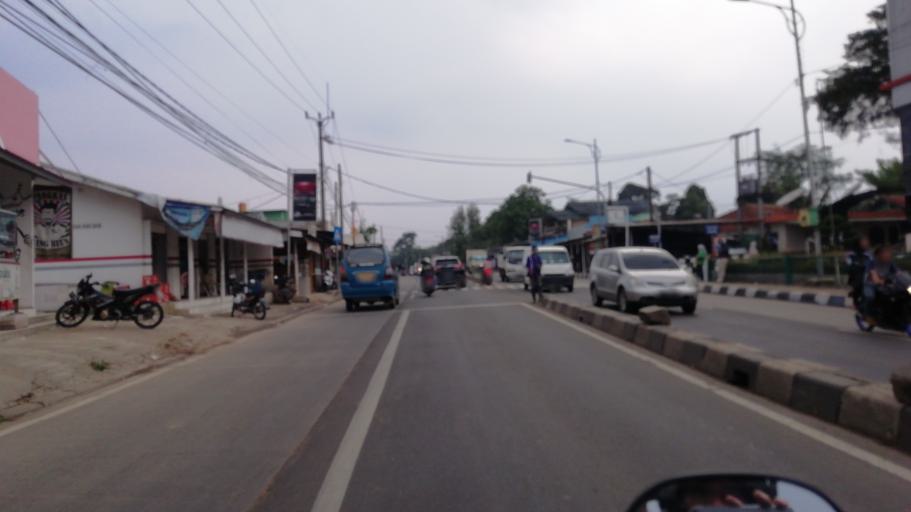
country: ID
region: West Java
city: Parung
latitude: -6.4948
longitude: 106.7513
